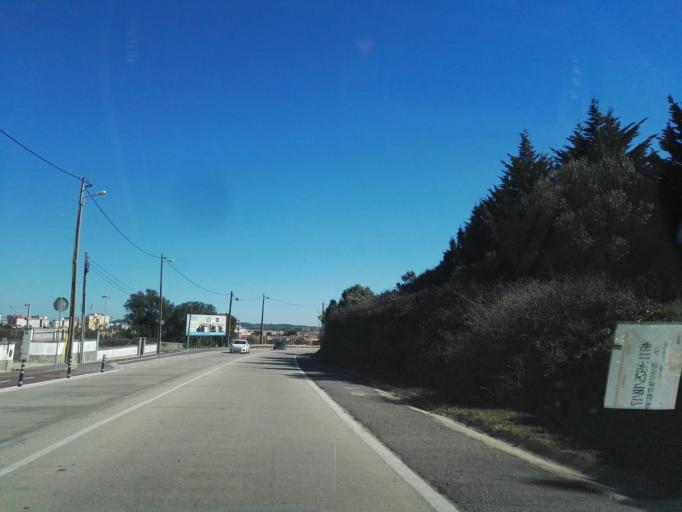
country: PT
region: Lisbon
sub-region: Sintra
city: Sintra
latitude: 38.8007
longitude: -9.3612
